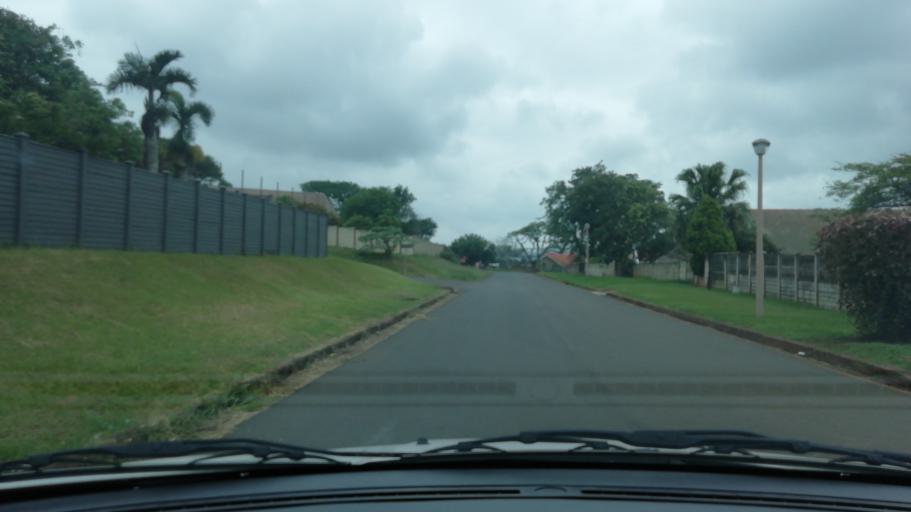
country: ZA
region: KwaZulu-Natal
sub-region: uThungulu District Municipality
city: Empangeni
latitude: -28.7628
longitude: 31.9026
